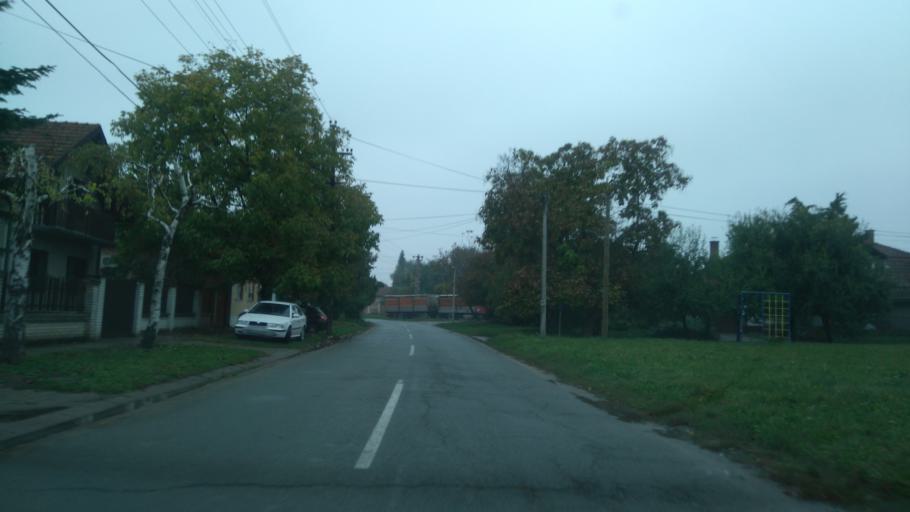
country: RS
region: Autonomna Pokrajina Vojvodina
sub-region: Juznobacki Okrug
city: Becej
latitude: 45.6231
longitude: 20.0548
